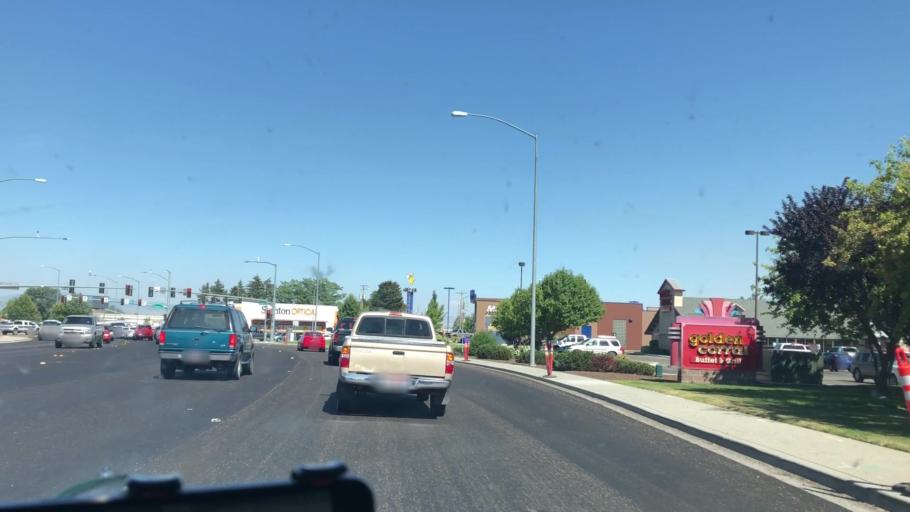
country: US
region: Idaho
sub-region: Canyon County
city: Nampa
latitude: 43.6049
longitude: -116.6046
